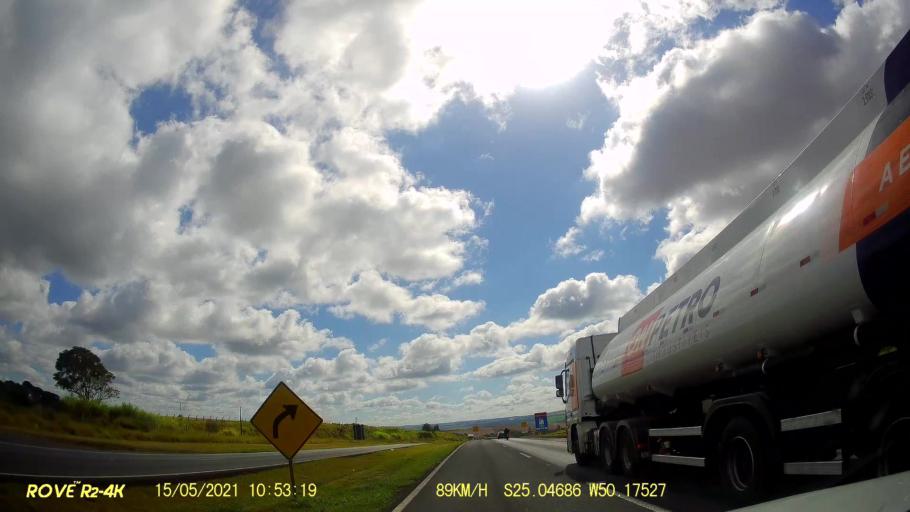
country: BR
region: Parana
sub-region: Ponta Grossa
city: Ponta Grossa
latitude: -25.0466
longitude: -50.1767
